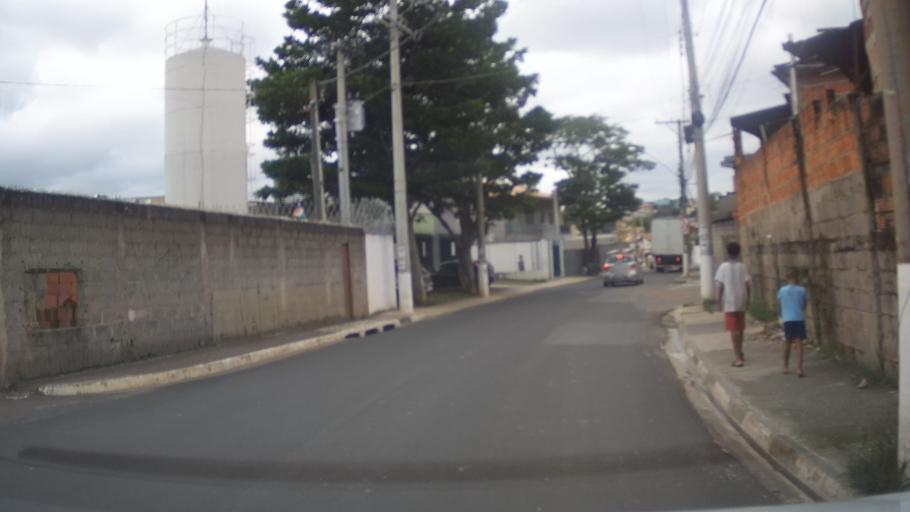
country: BR
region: Sao Paulo
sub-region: Louveira
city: Louveira
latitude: -23.0851
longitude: -46.9841
